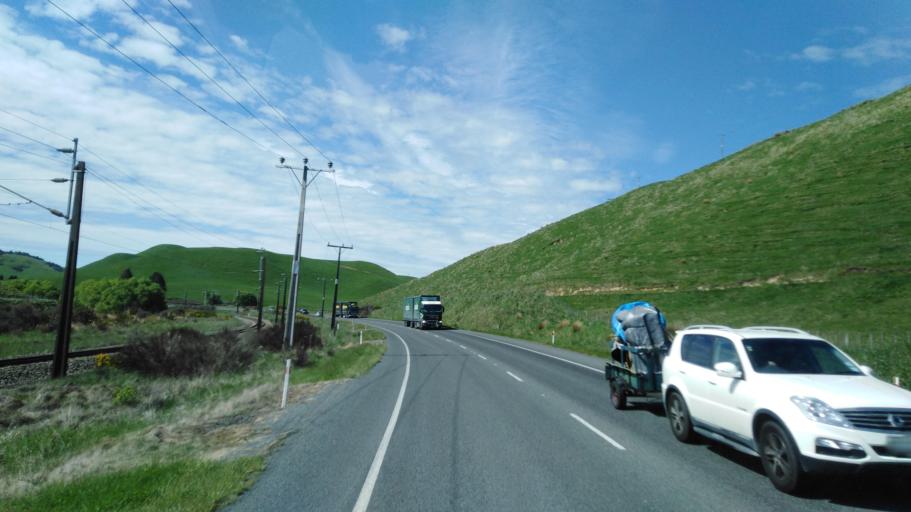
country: NZ
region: Manawatu-Wanganui
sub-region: Ruapehu District
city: Waiouru
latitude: -39.5036
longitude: 175.6740
